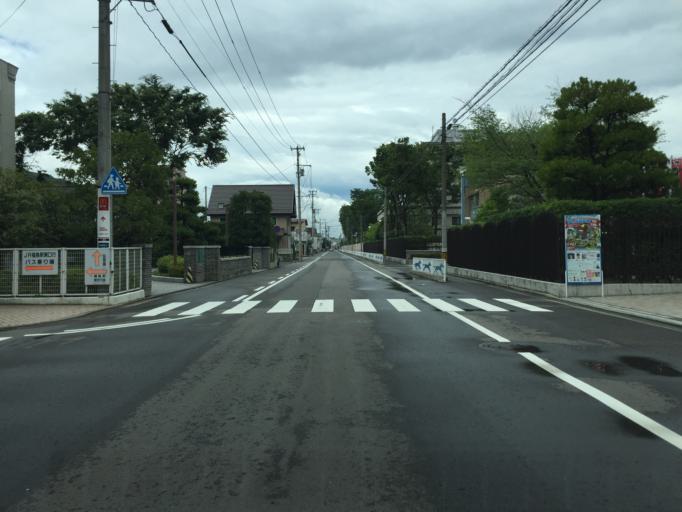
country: JP
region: Fukushima
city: Fukushima-shi
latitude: 37.7662
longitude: 140.4803
